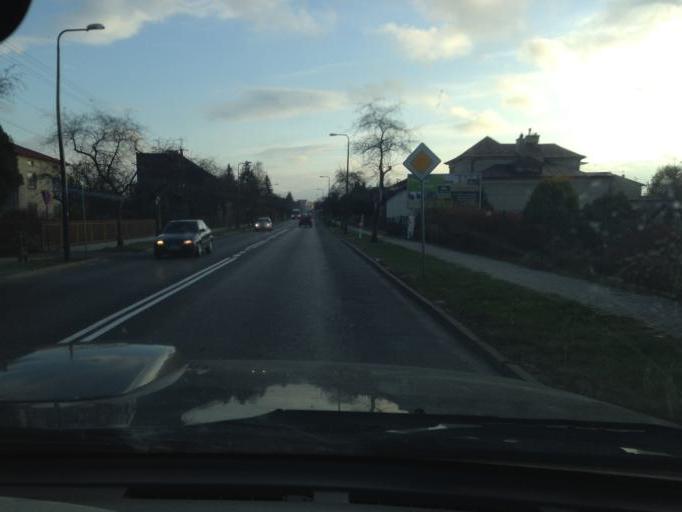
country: PL
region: Subcarpathian Voivodeship
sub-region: Powiat jasielski
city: Jaslo
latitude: 49.7586
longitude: 21.4714
